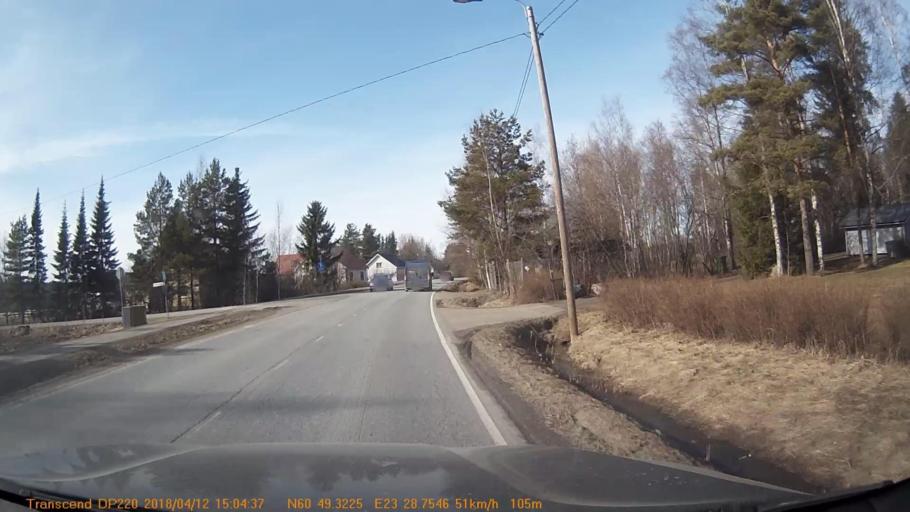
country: FI
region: Haeme
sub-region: Forssa
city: Jokioinen
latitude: 60.8222
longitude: 23.4790
